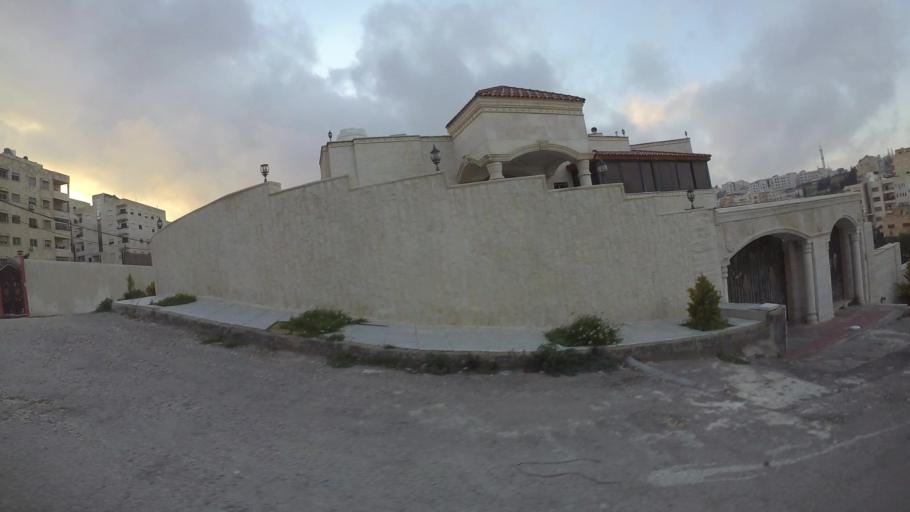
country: JO
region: Amman
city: Al Jubayhah
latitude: 32.0506
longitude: 35.8935
